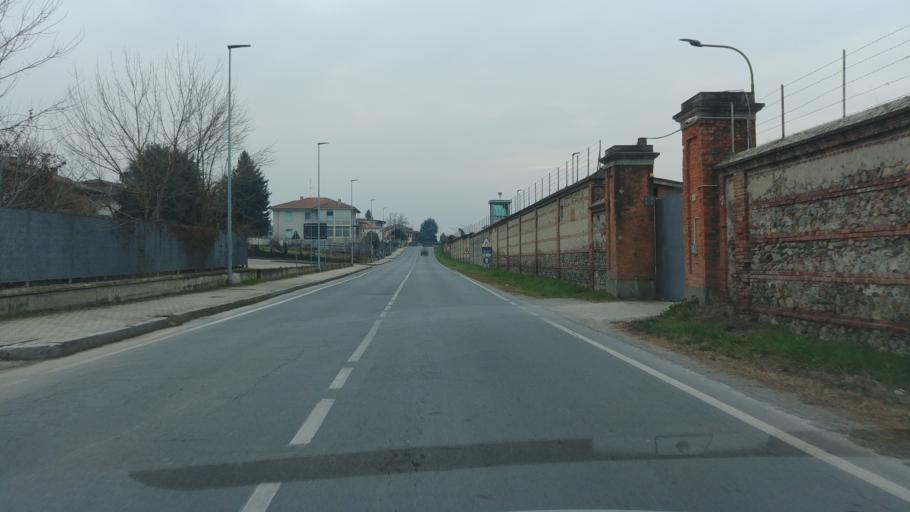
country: IT
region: Piedmont
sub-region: Provincia di Cuneo
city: Fossano
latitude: 44.5399
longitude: 7.7159
